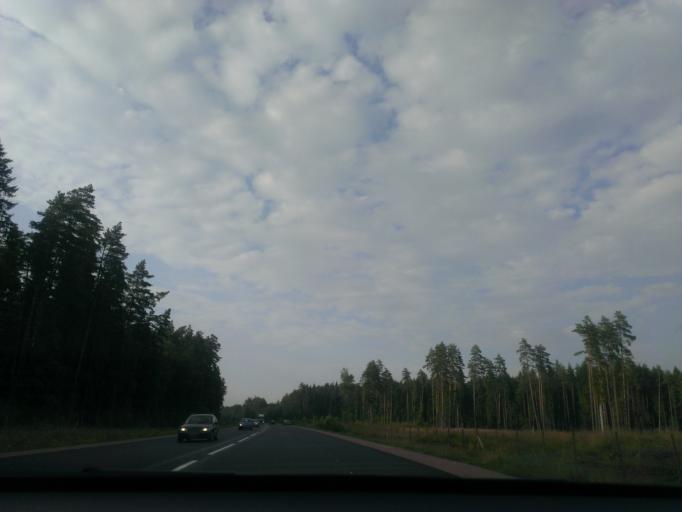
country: LV
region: Kekava
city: Kekava
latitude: 56.7230
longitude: 24.2533
